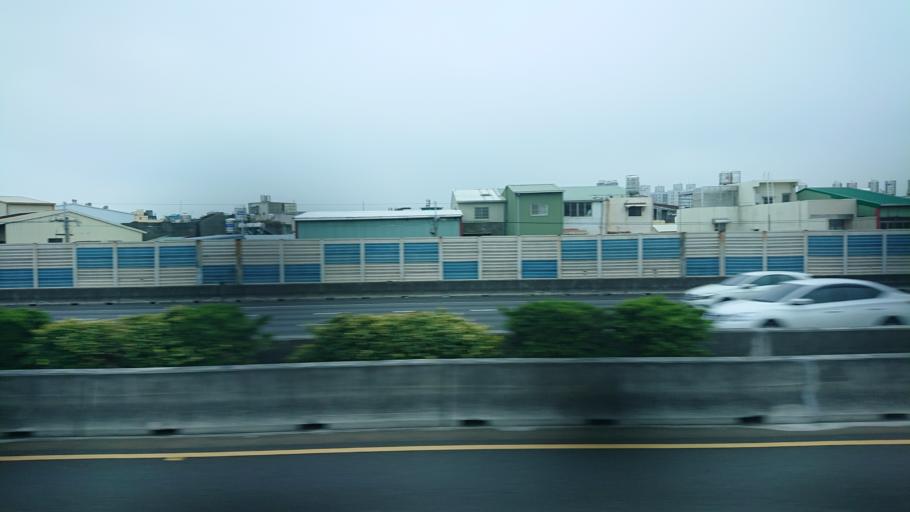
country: TW
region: Taiwan
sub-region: Changhua
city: Chang-hua
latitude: 24.0938
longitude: 120.5355
